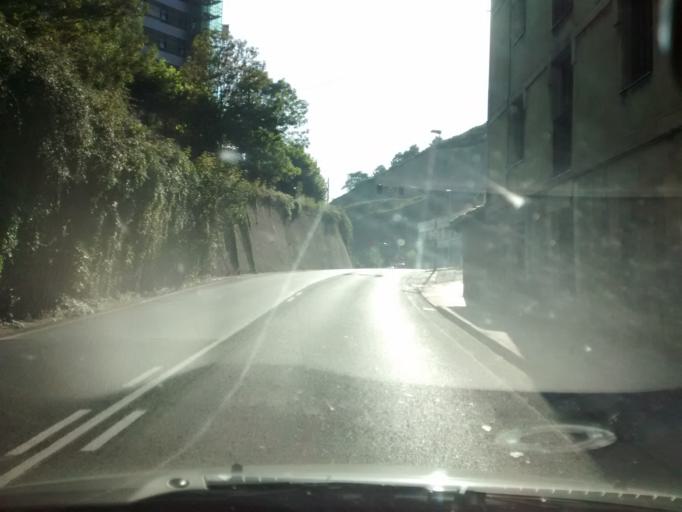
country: ES
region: Basque Country
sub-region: Bizkaia
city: Ermua
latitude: 43.1800
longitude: -2.4884
